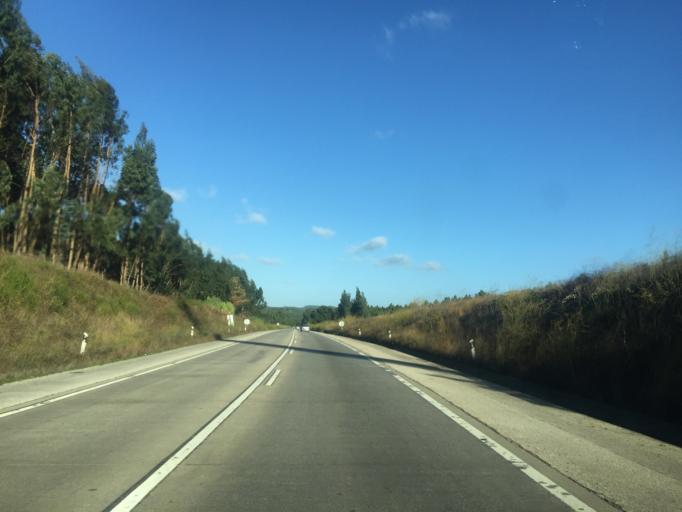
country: PT
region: Santarem
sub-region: Rio Maior
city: Rio Maior
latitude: 39.2860
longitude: -8.9421
